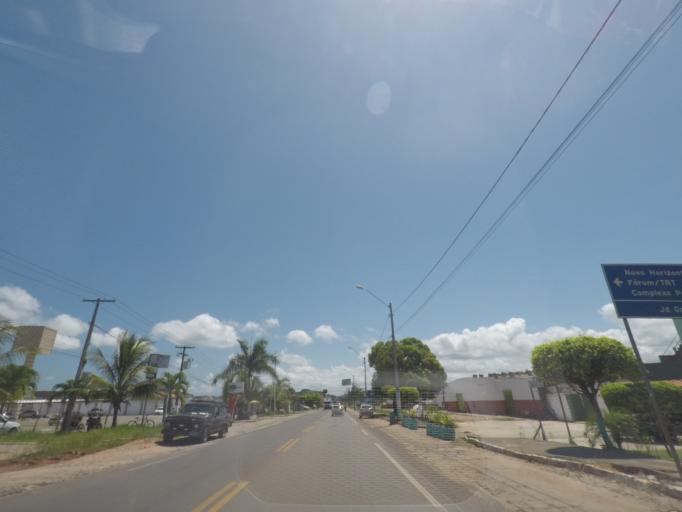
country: BR
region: Bahia
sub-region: Valenca
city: Valenca
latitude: -13.3500
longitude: -39.0609
